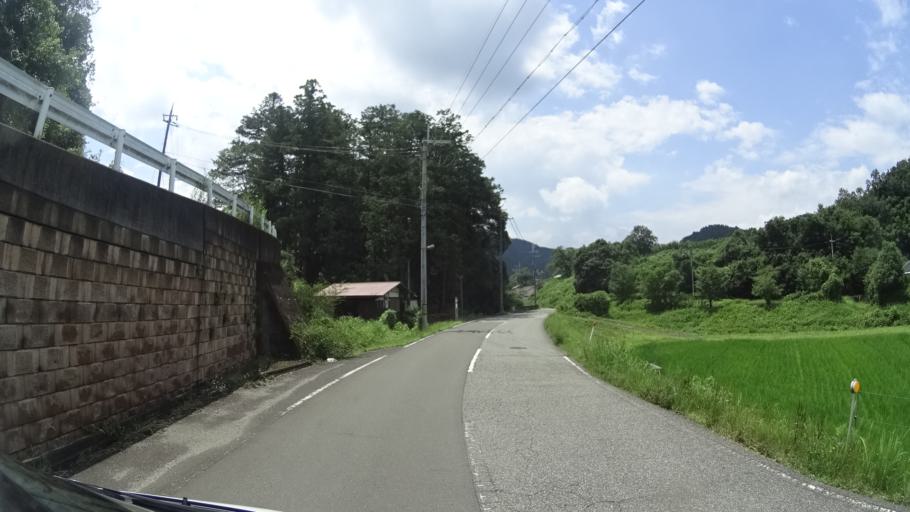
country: JP
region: Hyogo
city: Sasayama
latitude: 35.1722
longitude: 135.2758
